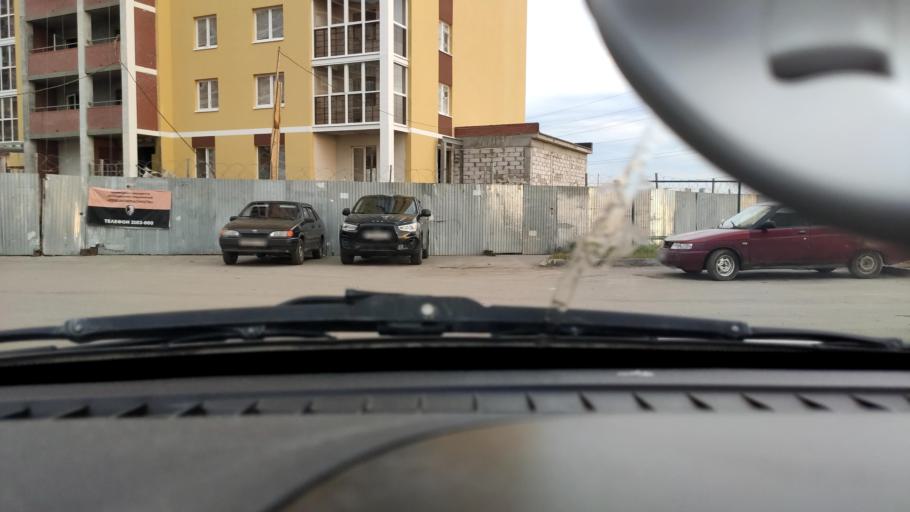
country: RU
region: Perm
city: Kondratovo
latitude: 58.0010
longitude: 56.1082
